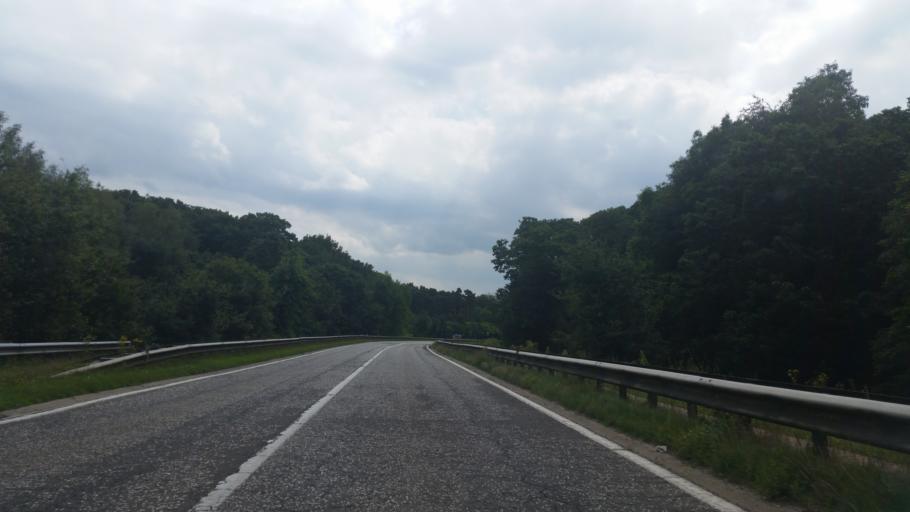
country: BE
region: Flanders
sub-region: Provincie Antwerpen
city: Vosselaar
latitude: 51.3268
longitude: 4.9136
